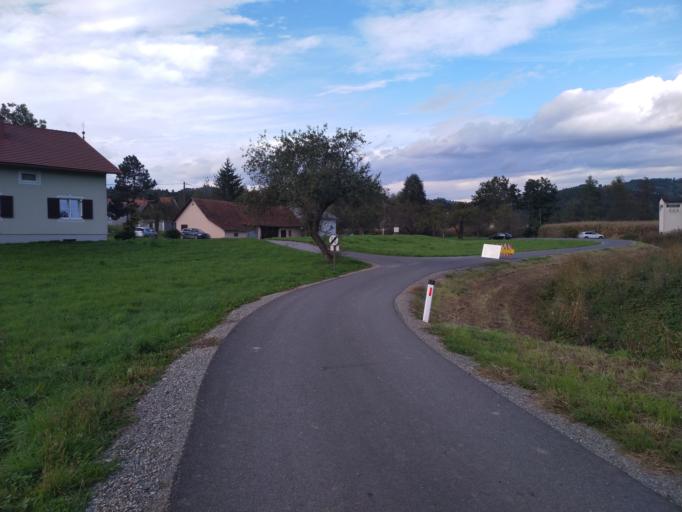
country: AT
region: Styria
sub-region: Politischer Bezirk Leibnitz
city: Grossklein
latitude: 46.7505
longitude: 15.4402
